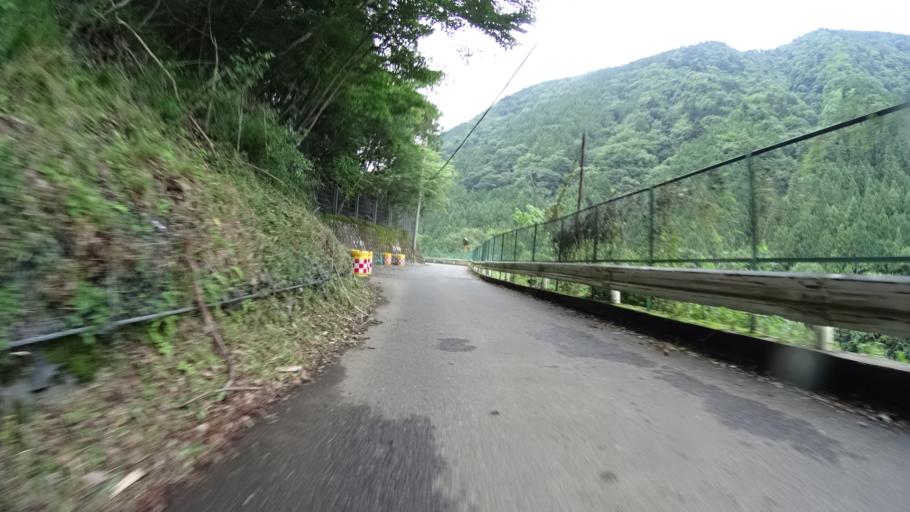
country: JP
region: Kanagawa
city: Hadano
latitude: 35.4879
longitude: 139.2214
